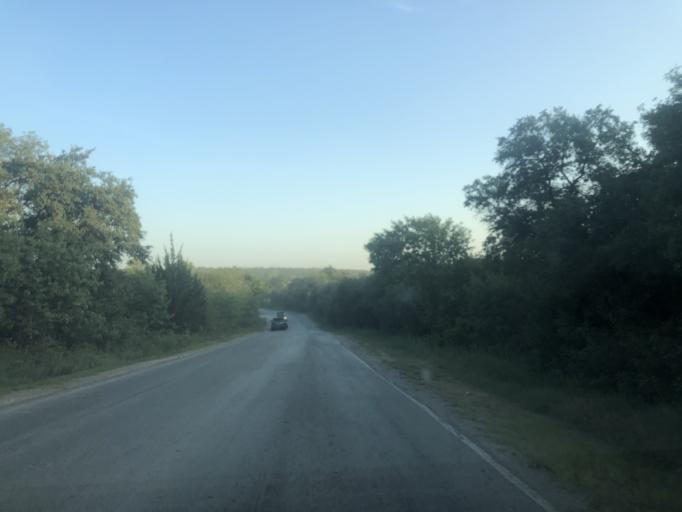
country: US
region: Texas
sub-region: Tarrant County
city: Lakeside
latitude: 32.7902
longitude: -97.4909
